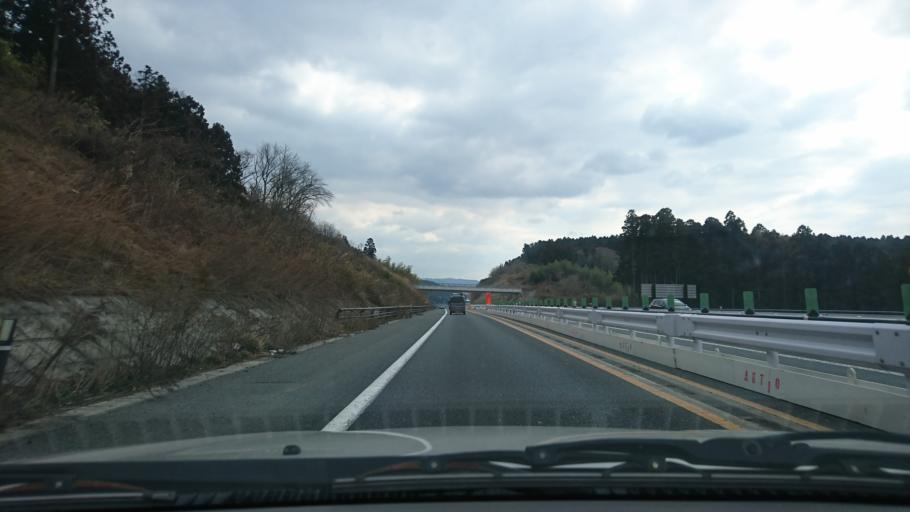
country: JP
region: Miyagi
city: Ishinomaki
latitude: 38.5402
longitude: 141.2763
